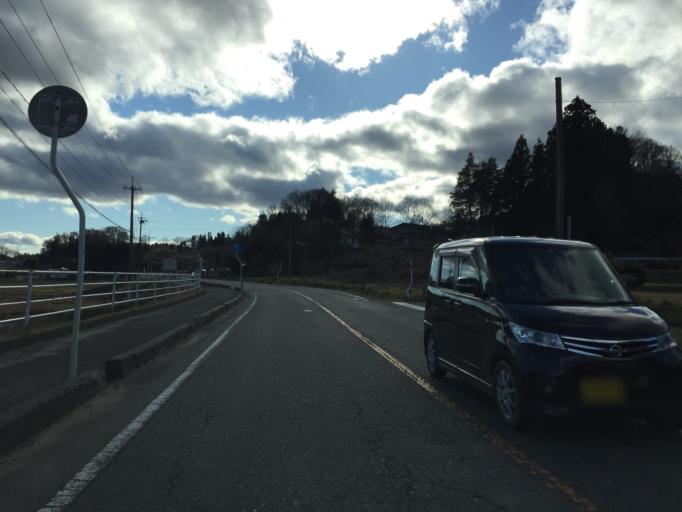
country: JP
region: Fukushima
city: Funehikimachi-funehiki
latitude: 37.5902
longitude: 140.5777
